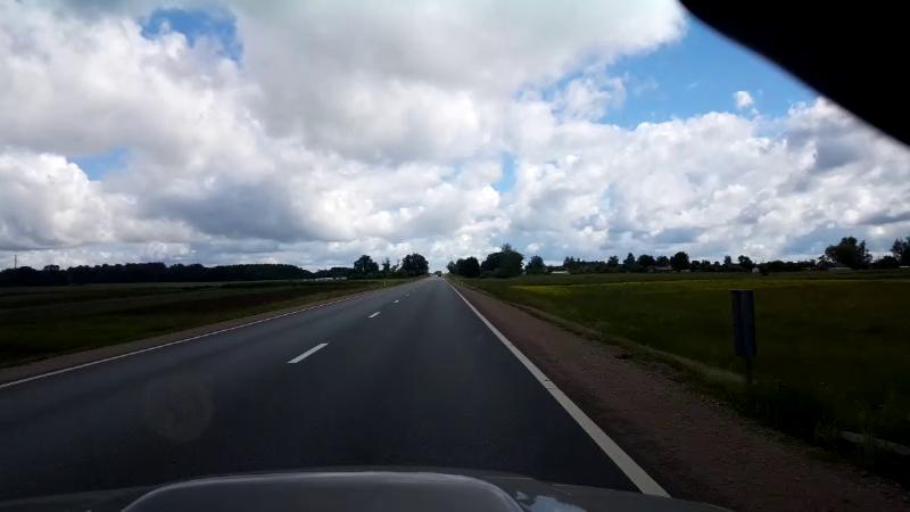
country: LV
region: Bauskas Rajons
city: Bauska
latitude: 56.4730
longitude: 24.1682
